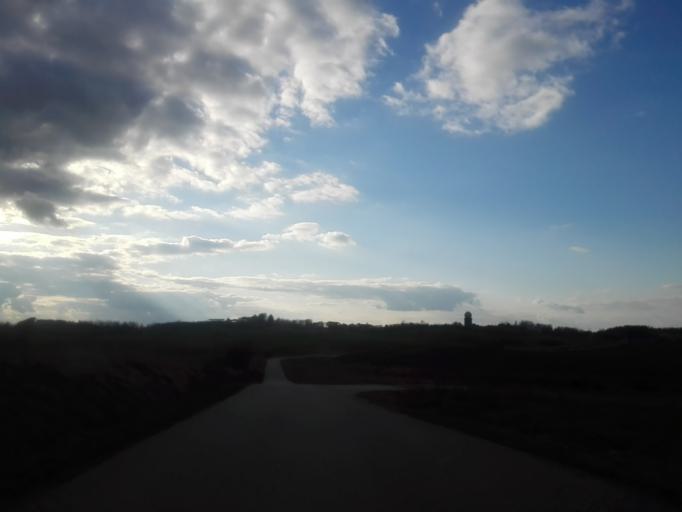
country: PL
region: Podlasie
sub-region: Suwalki
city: Suwalki
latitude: 54.2060
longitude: 23.0128
